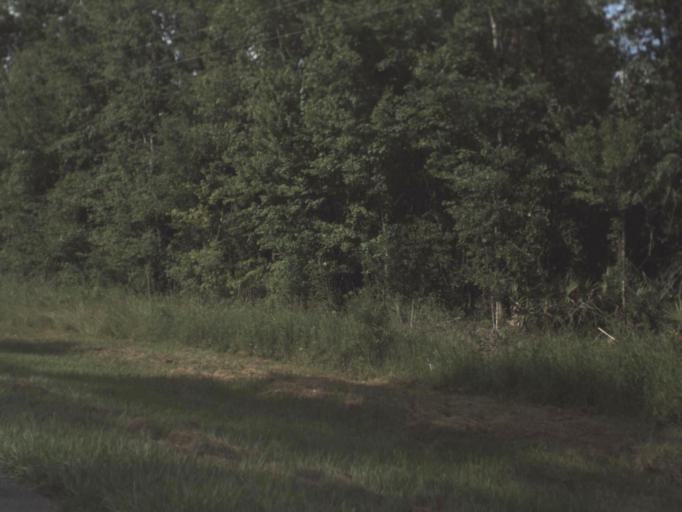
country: US
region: Florida
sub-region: Taylor County
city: Perry
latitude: 30.3384
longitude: -83.6457
